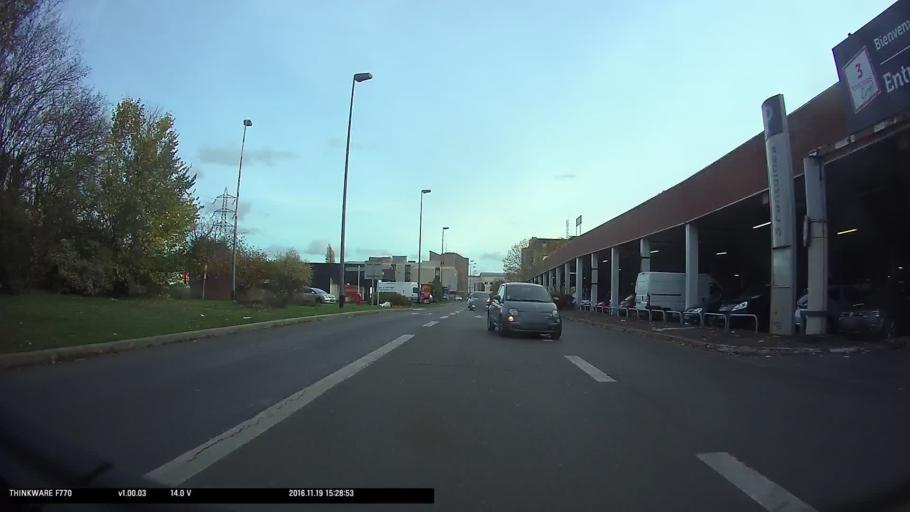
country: FR
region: Ile-de-France
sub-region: Departement du Val-d'Oise
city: Cergy-Pontoise
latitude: 49.0391
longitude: 2.0833
